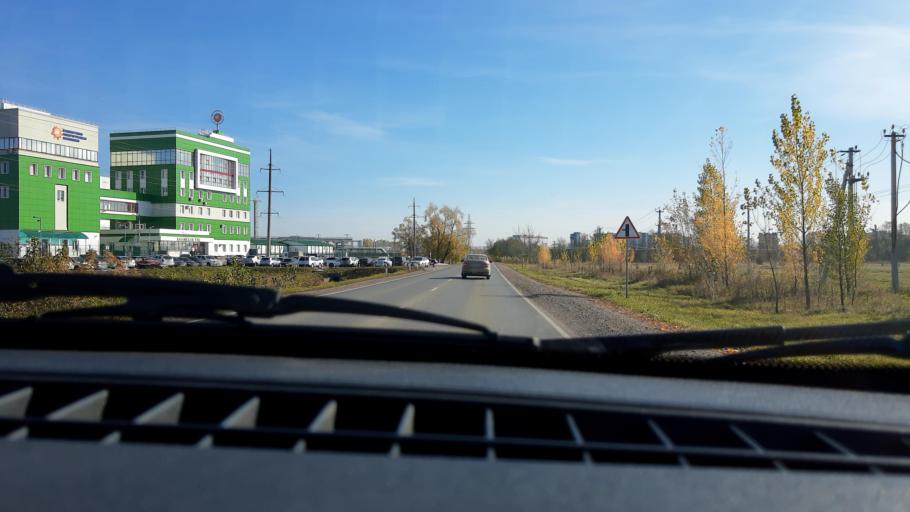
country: RU
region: Bashkortostan
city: Mikhaylovka
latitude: 54.8014
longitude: 55.8336
